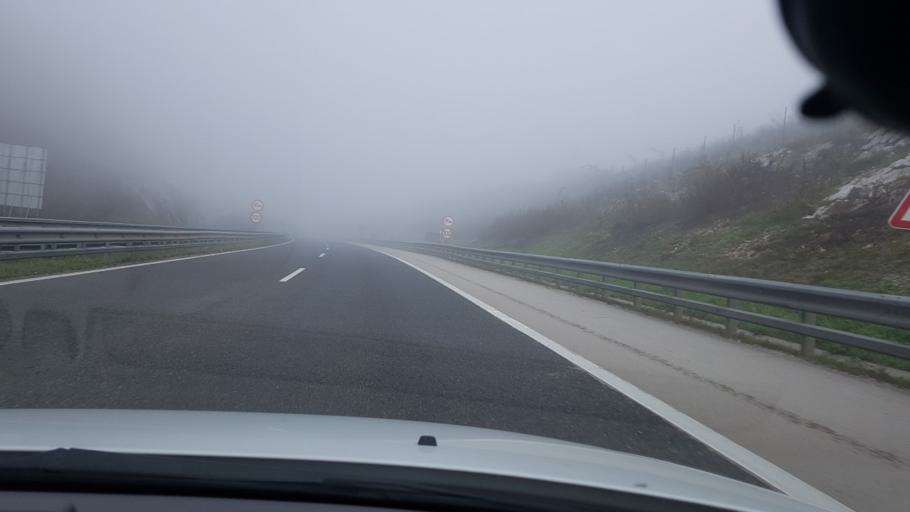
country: SI
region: Novo Mesto
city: Novo Mesto
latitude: 45.8497
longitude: 15.1466
